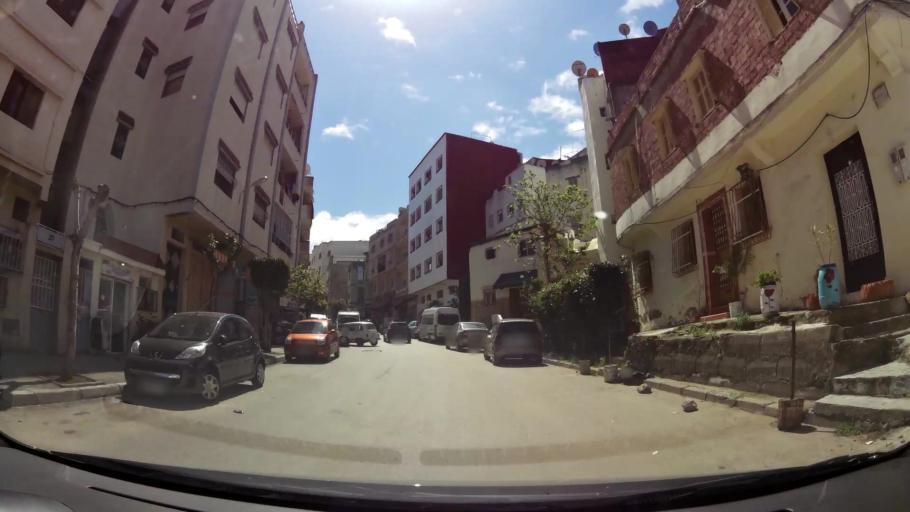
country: MA
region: Tanger-Tetouan
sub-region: Tanger-Assilah
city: Tangier
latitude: 35.7840
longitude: -5.8307
